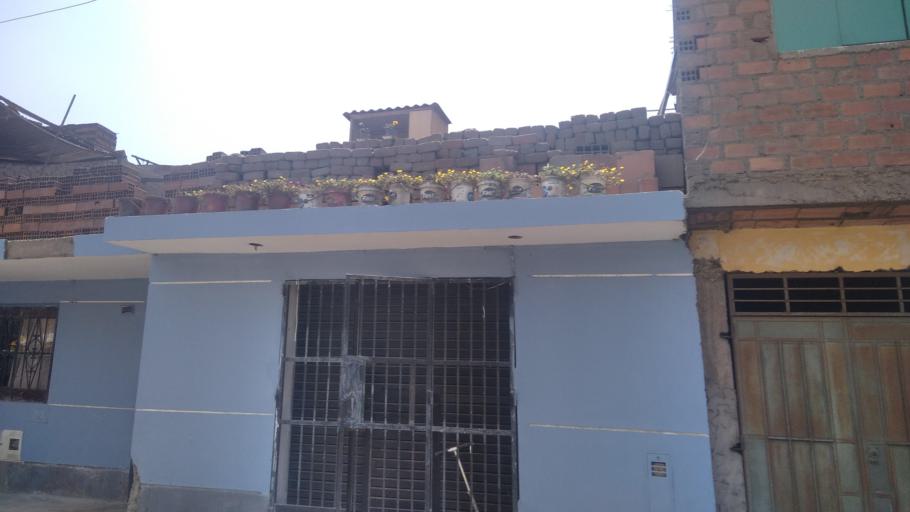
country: PE
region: Lima
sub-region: Lima
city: Independencia
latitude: -11.9637
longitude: -76.9795
